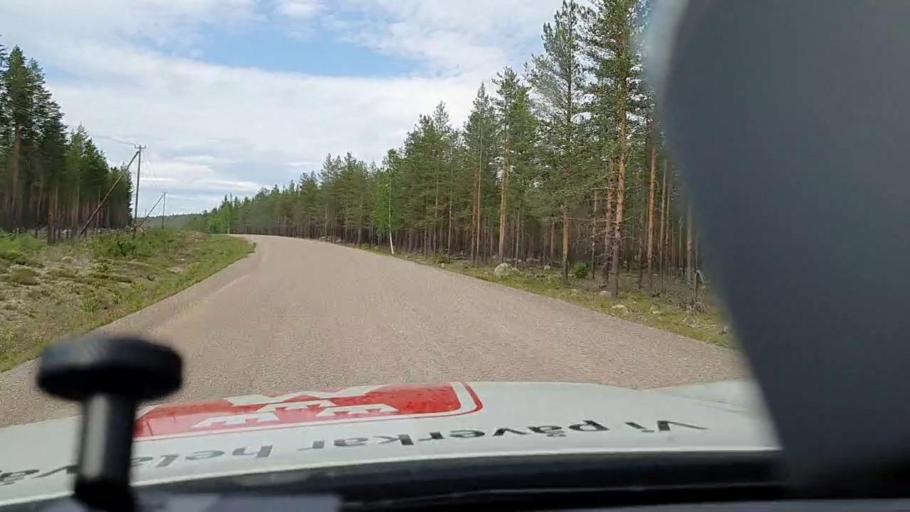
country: SE
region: Norrbotten
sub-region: Alvsbyns Kommun
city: AElvsbyn
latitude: 66.1222
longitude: 20.9920
